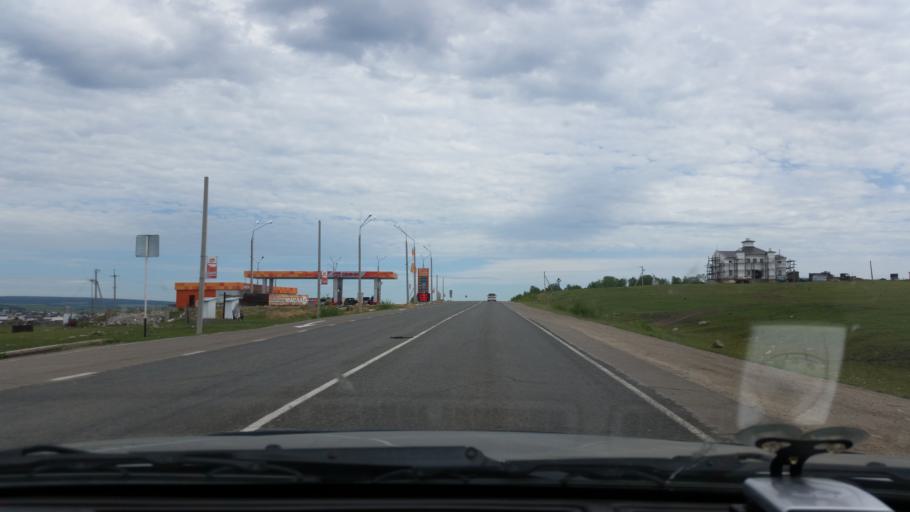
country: RU
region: Irkutsk
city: Bayanday
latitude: 53.0433
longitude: 105.5125
